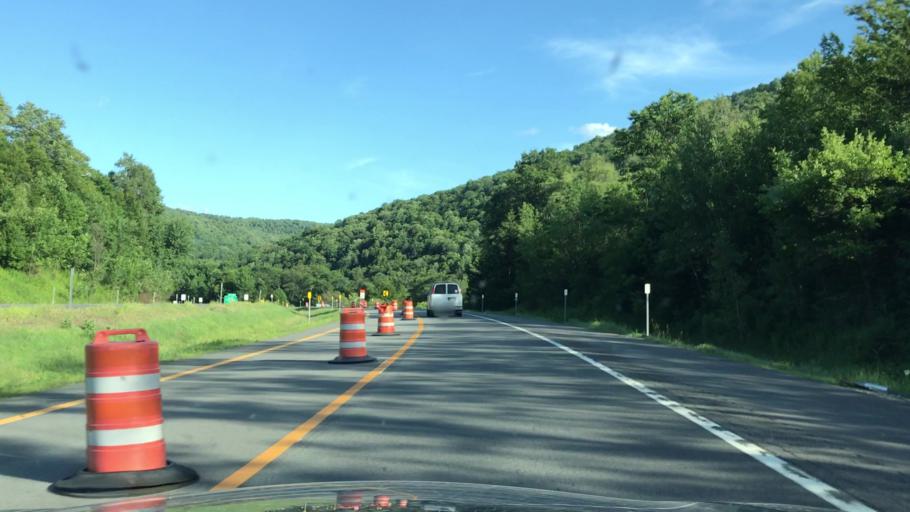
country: US
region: New York
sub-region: Delaware County
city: Walton
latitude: 41.9730
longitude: -75.0519
